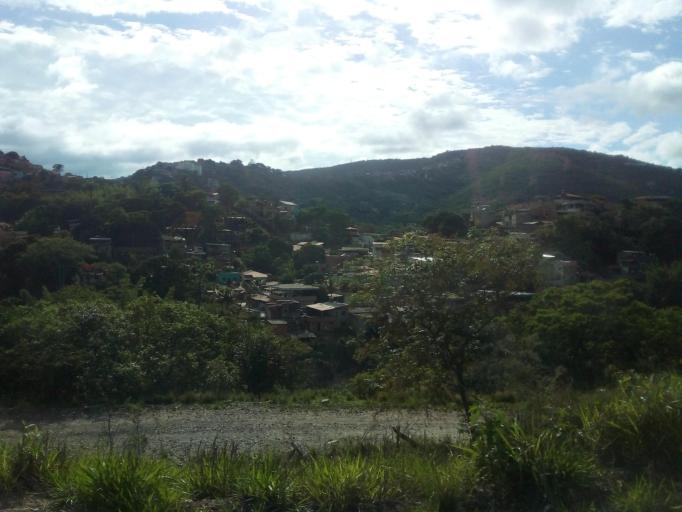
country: BR
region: Minas Gerais
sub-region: Belo Horizonte
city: Belo Horizonte
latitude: -19.8892
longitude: -43.8634
